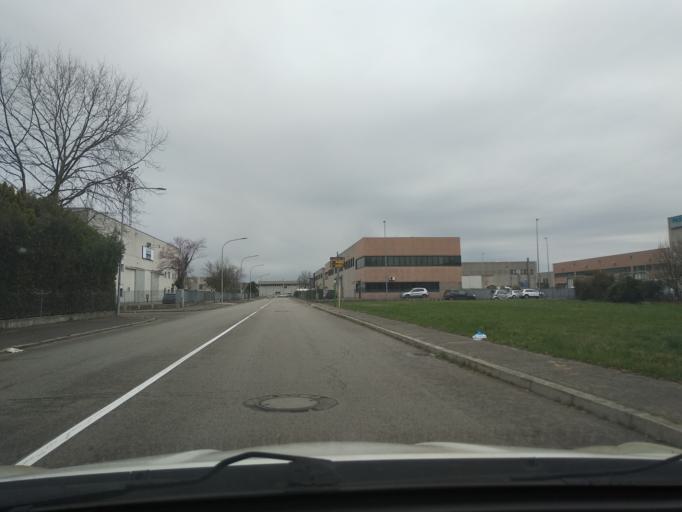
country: IT
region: Veneto
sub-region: Provincia di Padova
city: Rubano
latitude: 45.4211
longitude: 11.7949
